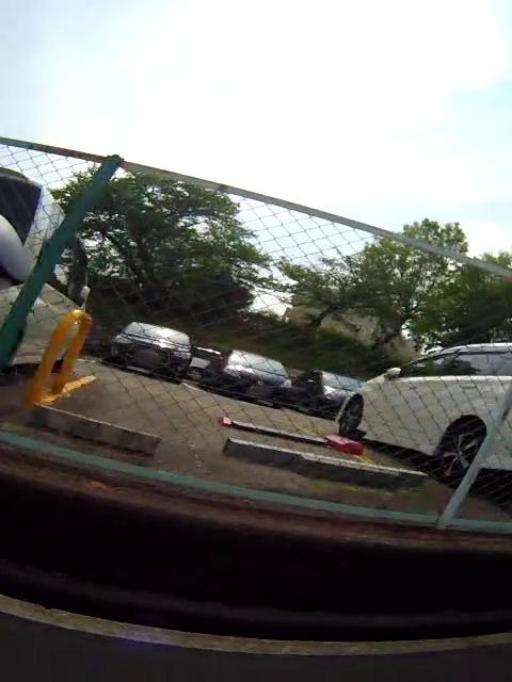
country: JP
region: Osaka
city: Toyonaka
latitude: 34.7858
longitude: 135.4822
